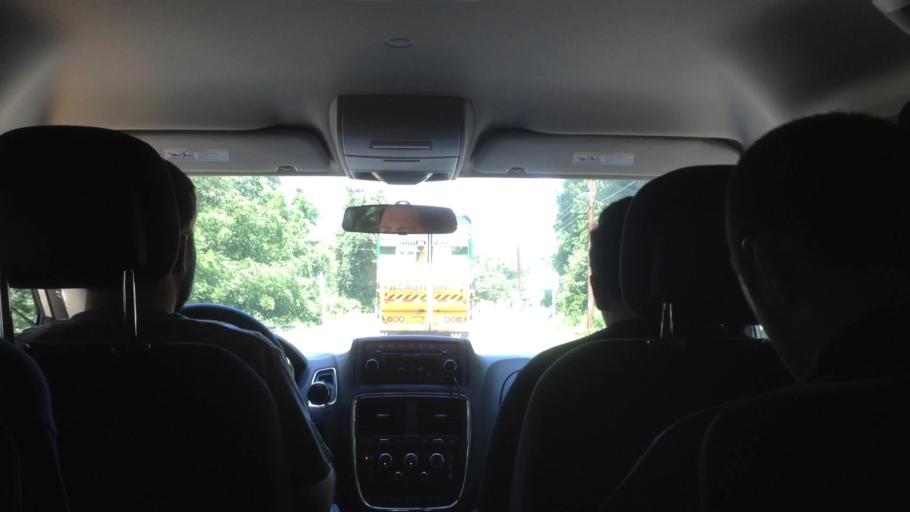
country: US
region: New York
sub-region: Dutchess County
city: Red Hook
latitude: 42.0395
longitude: -73.8490
